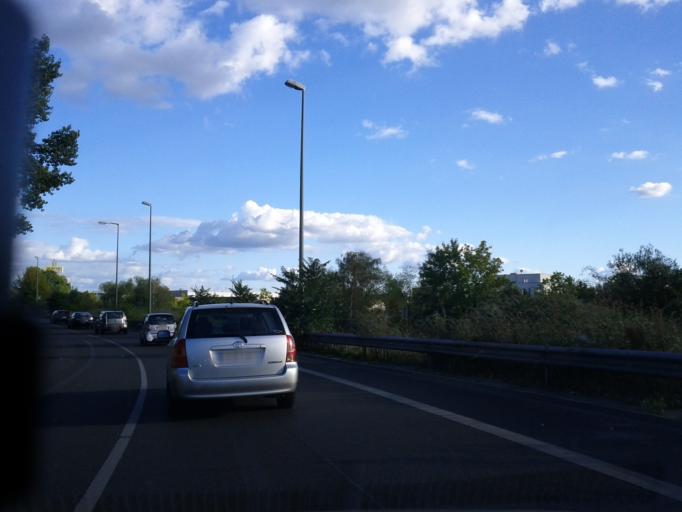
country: DE
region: Berlin
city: Friedrichshain Bezirk
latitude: 52.5258
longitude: 13.4593
